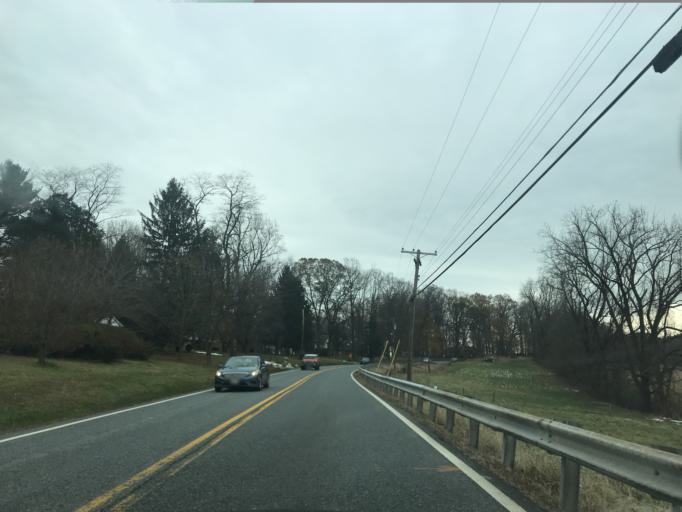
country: US
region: Maryland
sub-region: Harford County
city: Bel Air North
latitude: 39.6104
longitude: -76.3324
